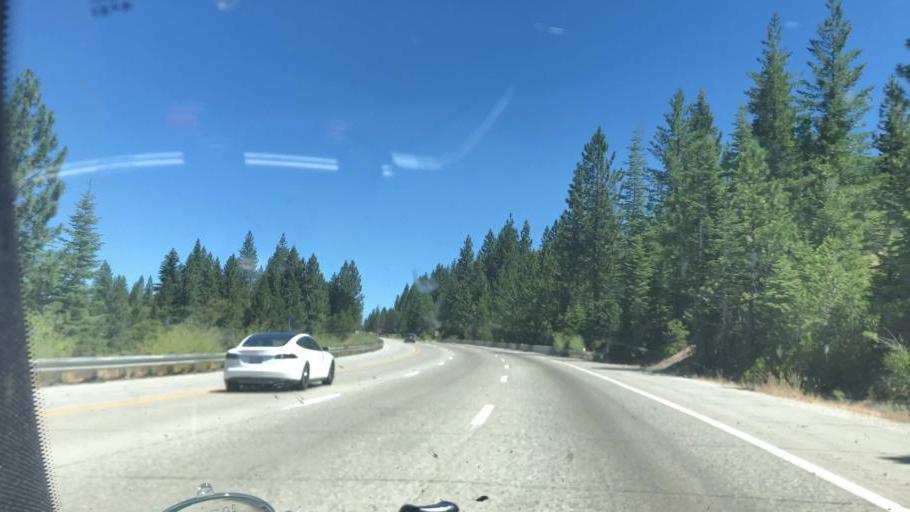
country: US
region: California
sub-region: Placer County
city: Foresthill
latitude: 39.2564
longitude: -120.7320
